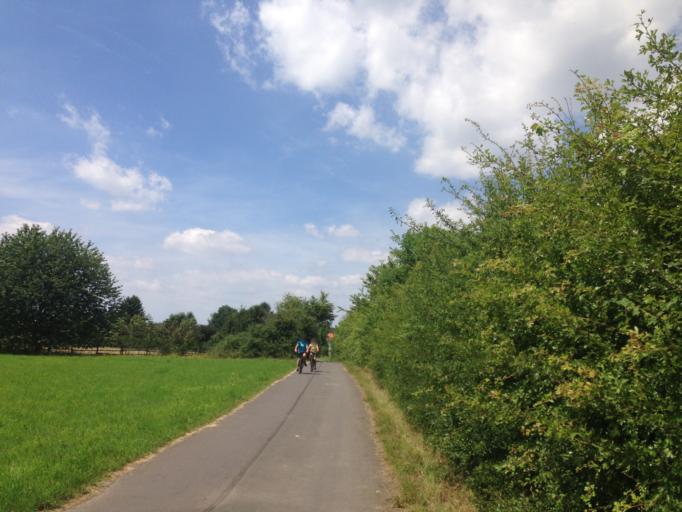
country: DE
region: Hesse
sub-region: Regierungsbezirk Giessen
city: Reiskirchen
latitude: 50.5983
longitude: 8.8417
